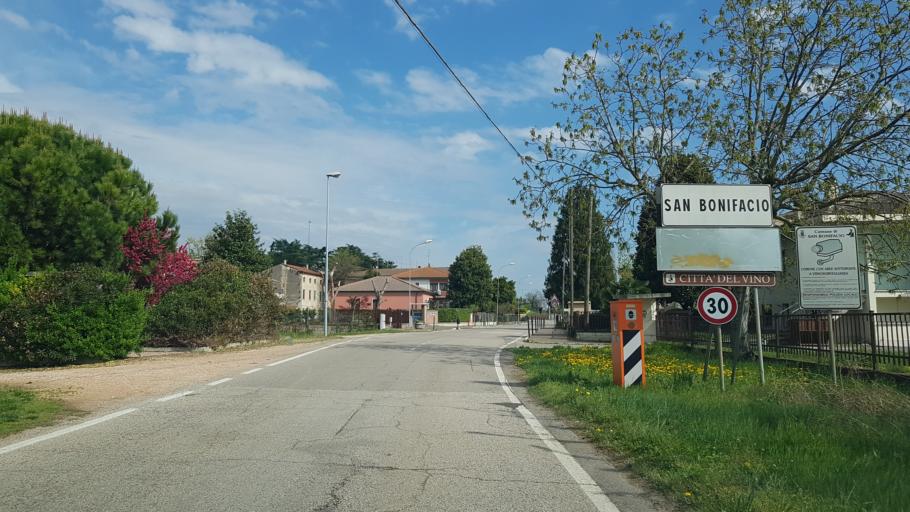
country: IT
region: Veneto
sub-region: Provincia di Verona
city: San Bonifacio
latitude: 45.3929
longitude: 11.2613
